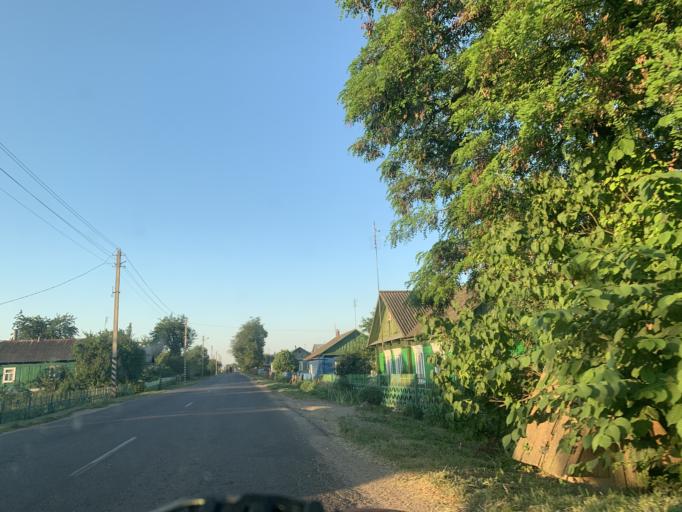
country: BY
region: Minsk
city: Haradzyeya
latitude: 53.2453
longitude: 26.5080
